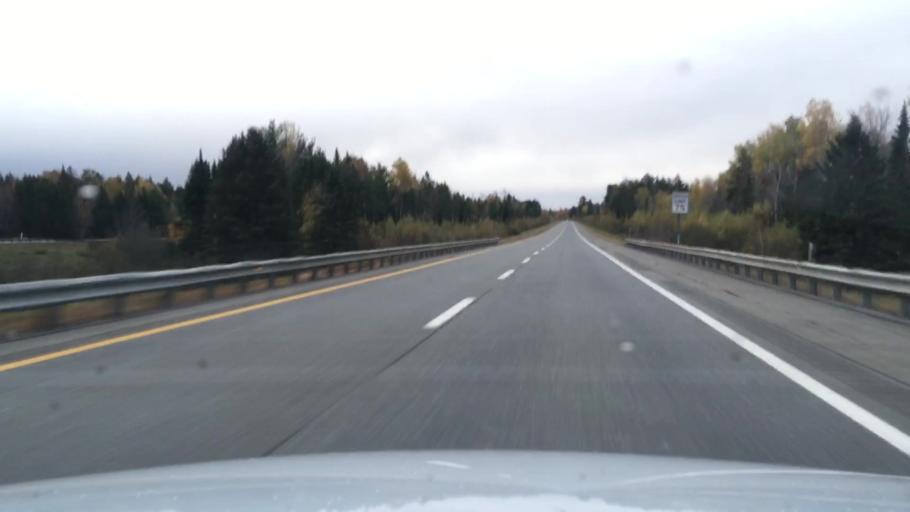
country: US
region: Maine
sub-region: Penobscot County
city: Greenbush
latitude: 45.1096
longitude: -68.6955
